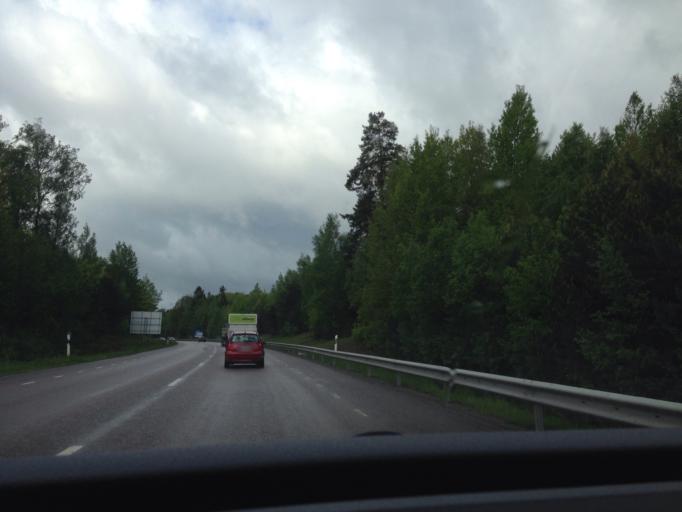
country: SE
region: Vaestra Goetaland
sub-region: Skovde Kommun
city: Skoevde
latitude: 58.4058
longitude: 13.8747
